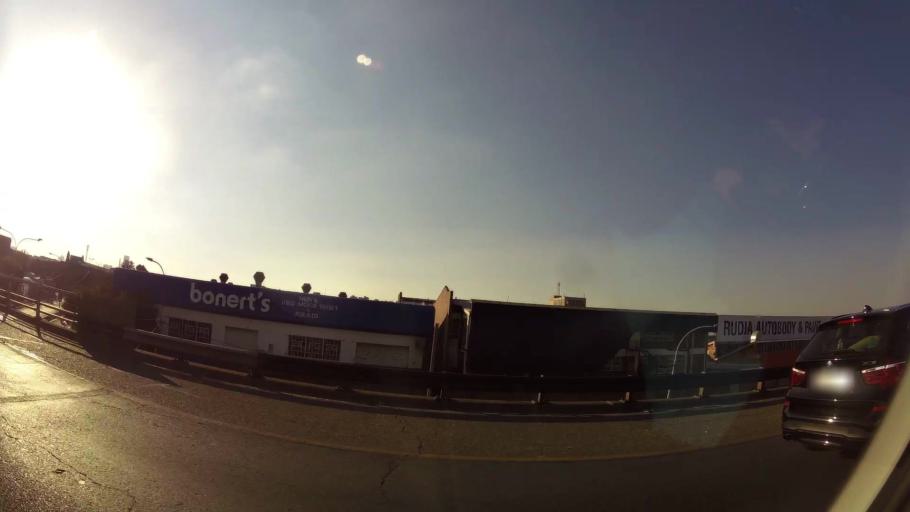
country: ZA
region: Gauteng
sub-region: City of Johannesburg Metropolitan Municipality
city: Johannesburg
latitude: -26.2126
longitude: 28.0757
